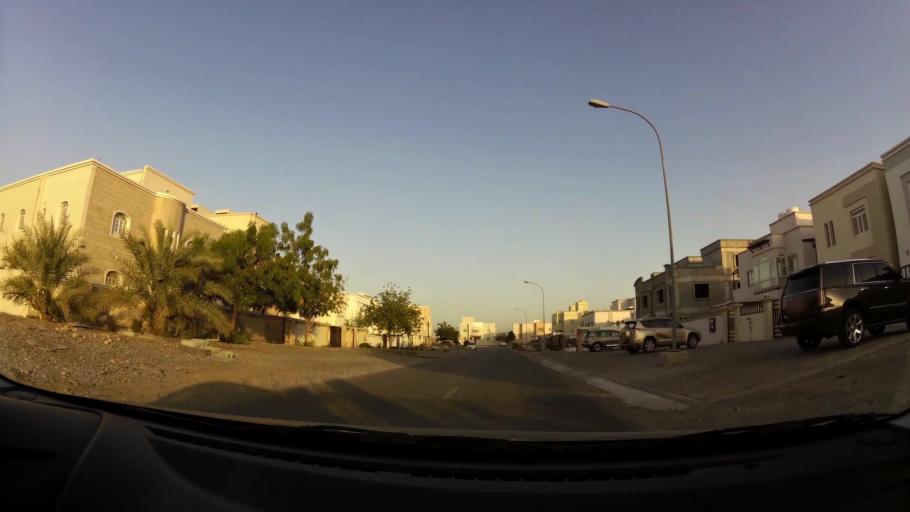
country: OM
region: Muhafazat Masqat
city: As Sib al Jadidah
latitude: 23.6111
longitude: 58.1968
